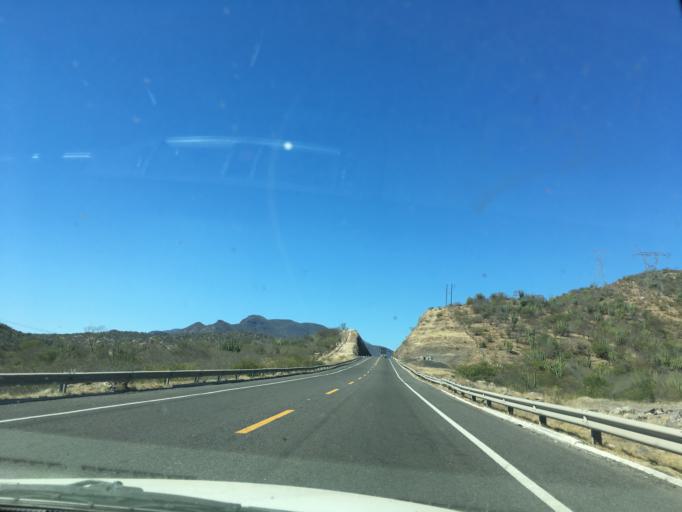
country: MX
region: Michoacan
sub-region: Arteaga
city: Las Canas
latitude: 18.4931
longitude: -101.9700
